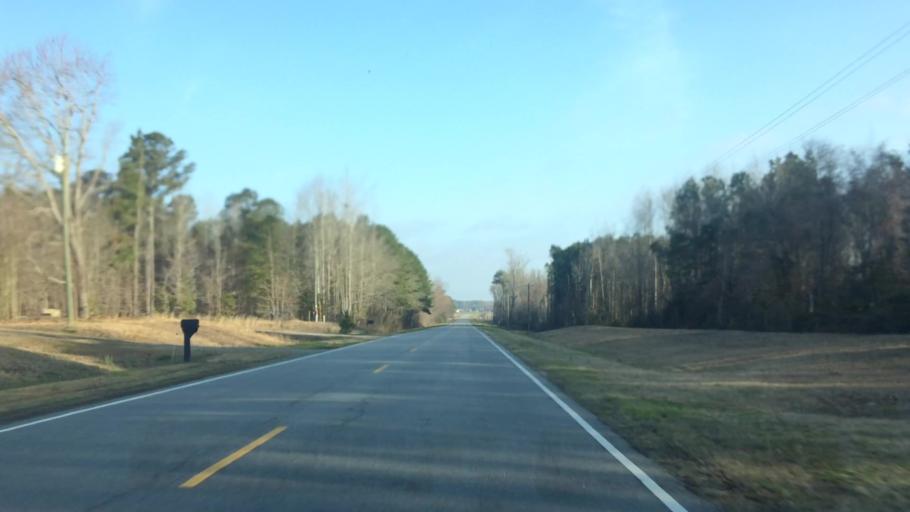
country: US
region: North Carolina
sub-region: Edgecombe County
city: Pinetops
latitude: 35.7158
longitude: -77.6335
